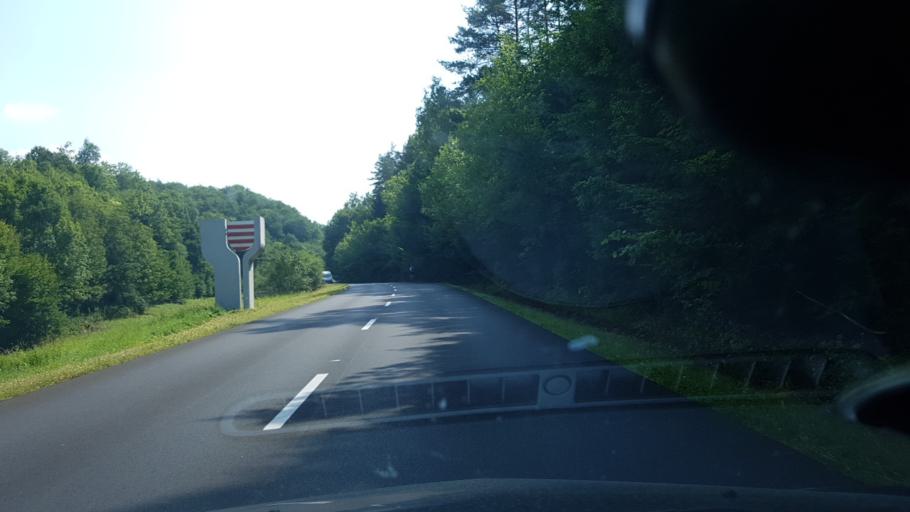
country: SK
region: Banskobystricky
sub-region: Okres Banska Bystrica
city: Banska Bystrica
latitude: 48.7157
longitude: 19.1793
